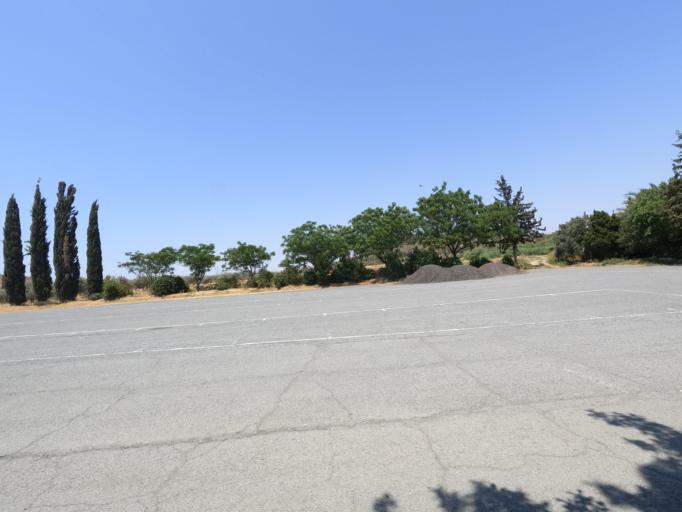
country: CY
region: Larnaka
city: Troulloi
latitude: 35.0141
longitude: 33.6330
